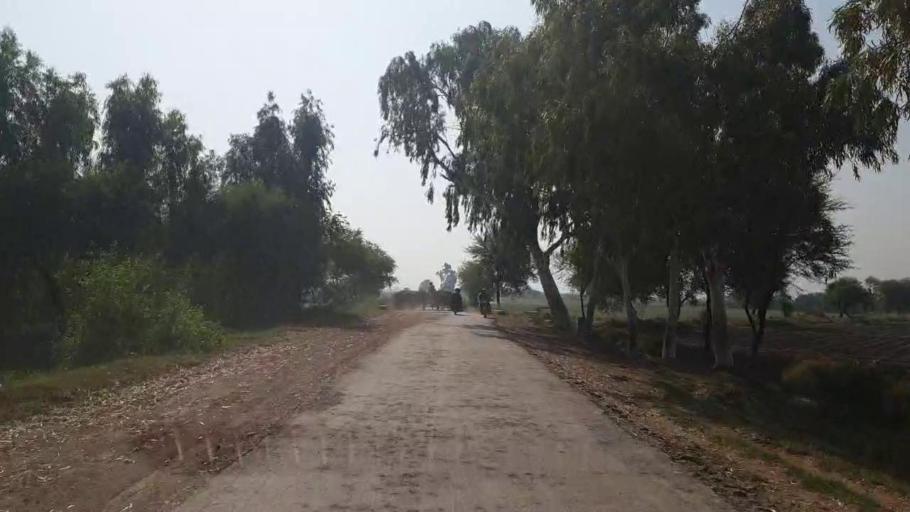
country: PK
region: Sindh
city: Shahdadpur
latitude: 25.9276
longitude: 68.7329
